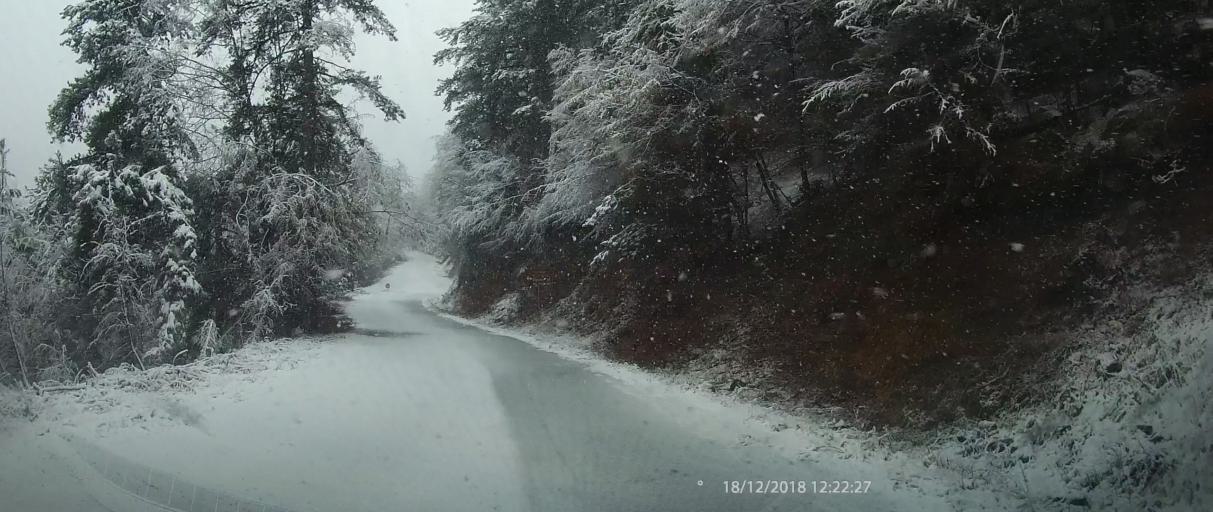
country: GR
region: Central Macedonia
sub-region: Nomos Pierias
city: Litochoro
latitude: 40.0942
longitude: 22.4200
